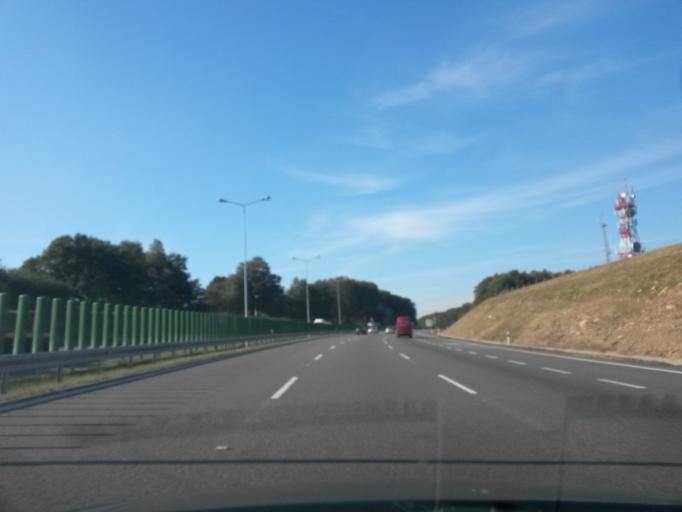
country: PL
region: Opole Voivodeship
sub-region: Powiat strzelecki
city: Lesnica
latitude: 50.4634
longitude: 18.1557
